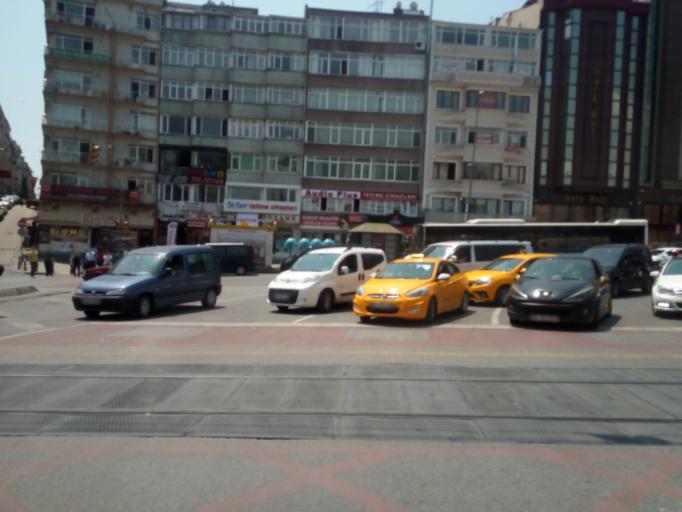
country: TR
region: Istanbul
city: Istanbul
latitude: 41.0121
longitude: 28.9398
